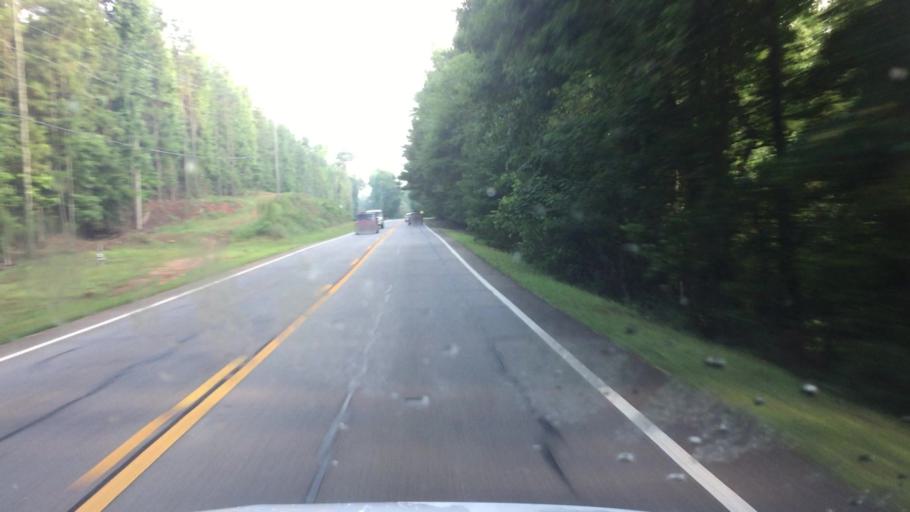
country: US
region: Georgia
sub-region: DeKalb County
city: Pine Mountain
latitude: 33.6195
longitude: -84.1711
